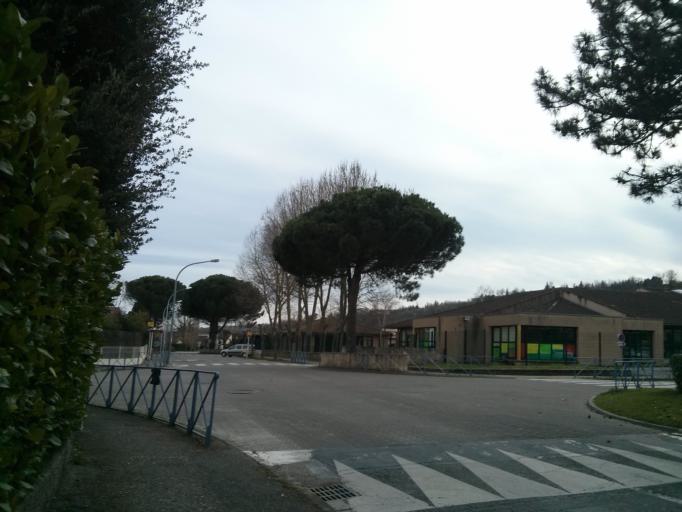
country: FR
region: Midi-Pyrenees
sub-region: Departement de la Haute-Garonne
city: Castanet-Tolosan
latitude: 43.5150
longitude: 1.5037
